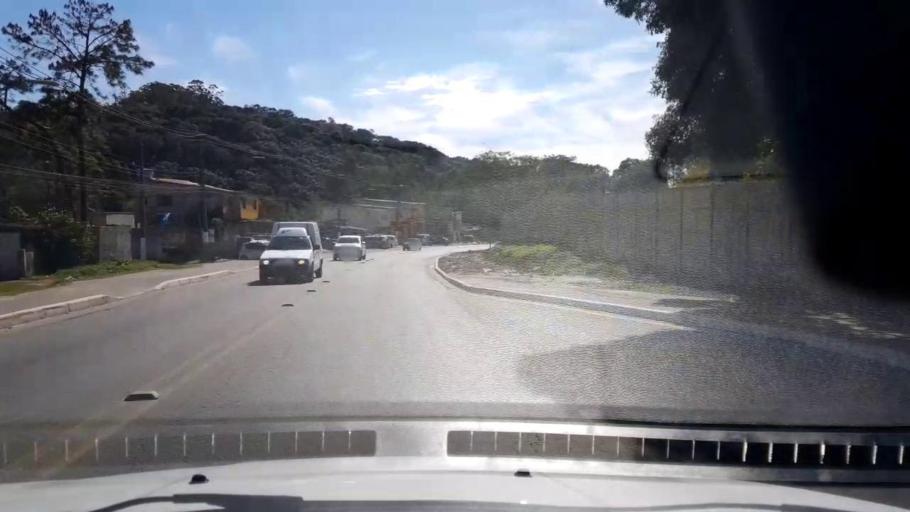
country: BR
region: Sao Paulo
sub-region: Ferraz De Vasconcelos
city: Ferraz de Vasconcelos
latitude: -23.5773
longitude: -46.4161
